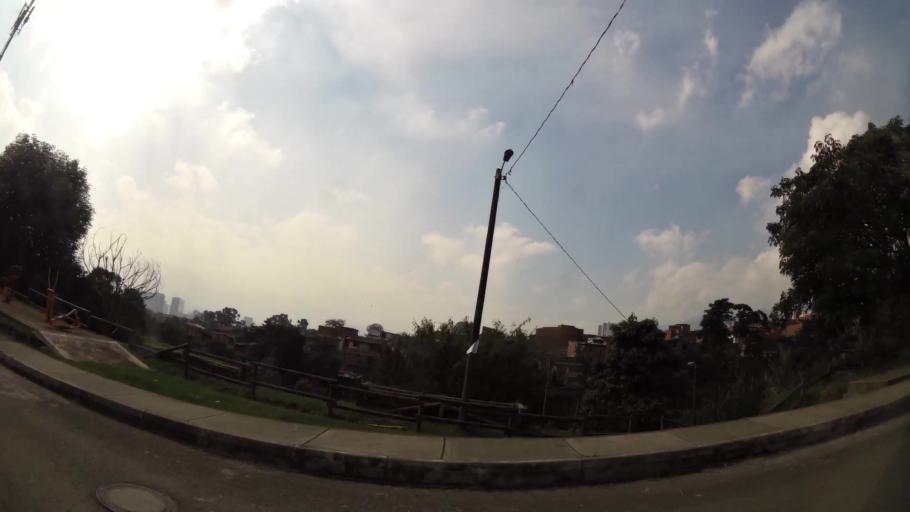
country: CO
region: Antioquia
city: La Estrella
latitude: 6.1744
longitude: -75.6448
